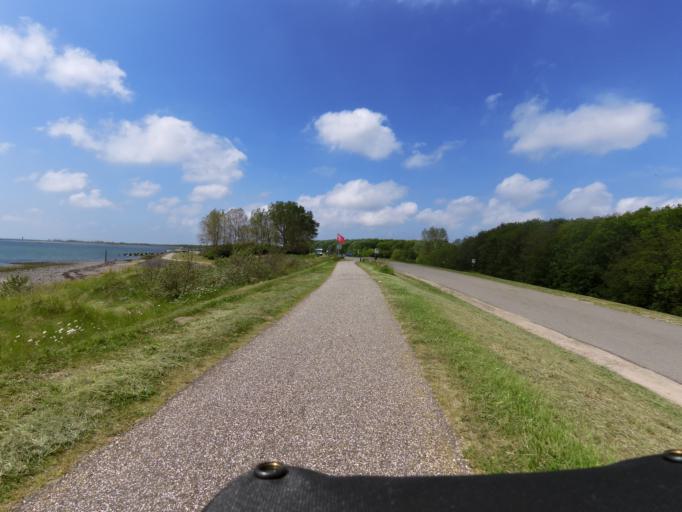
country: NL
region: Zeeland
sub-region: Schouwen-Duiveland
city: Scharendijke
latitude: 51.6980
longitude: 3.8138
